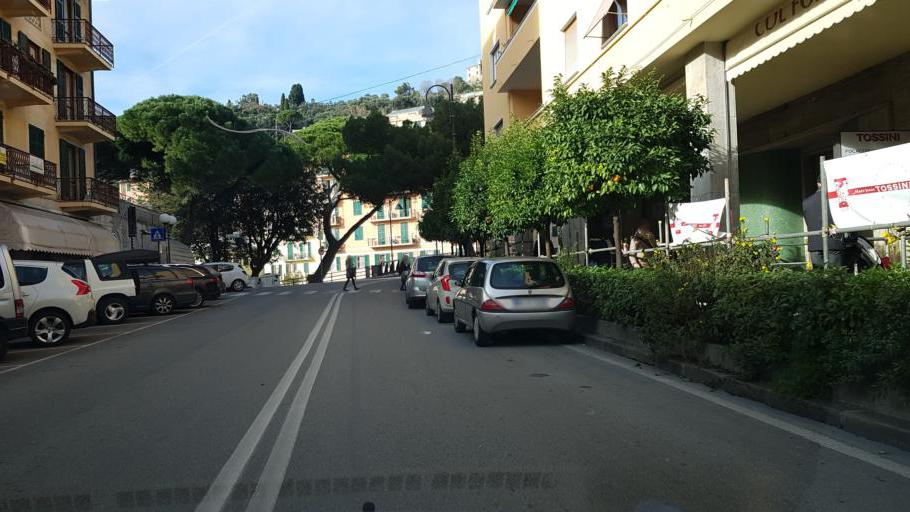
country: IT
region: Liguria
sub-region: Provincia di Genova
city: Recco
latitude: 44.3618
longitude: 9.1427
